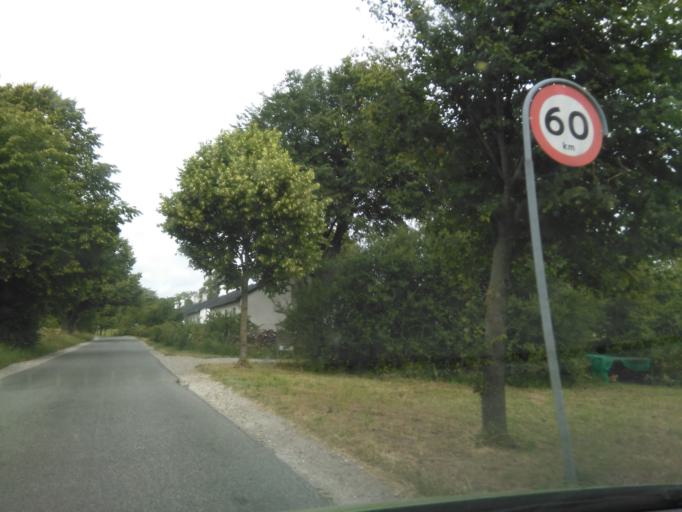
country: DK
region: Central Jutland
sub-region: Arhus Kommune
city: Beder
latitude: 56.0638
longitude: 10.1939
